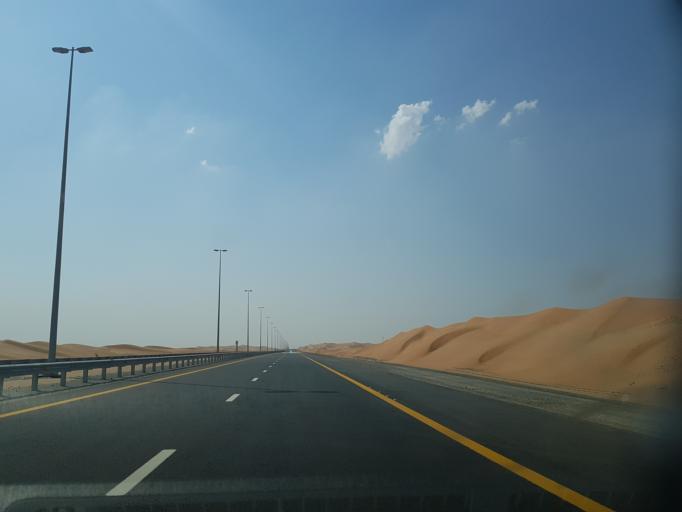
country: AE
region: Ash Shariqah
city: Adh Dhayd
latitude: 25.2571
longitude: 55.7190
